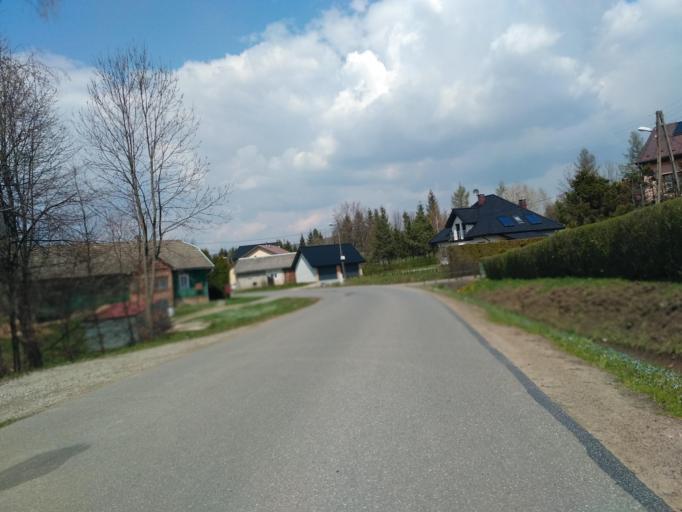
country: PL
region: Subcarpathian Voivodeship
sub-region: Powiat sanocki
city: Nowosielce-Gniewosz
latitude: 49.5445
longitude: 22.1096
